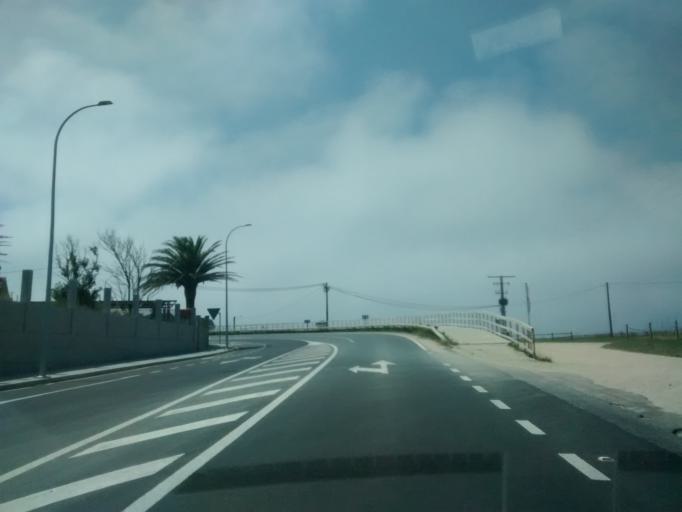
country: ES
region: Galicia
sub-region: Provincia de Pontevedra
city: O Grove
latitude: 42.4294
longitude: -8.8732
